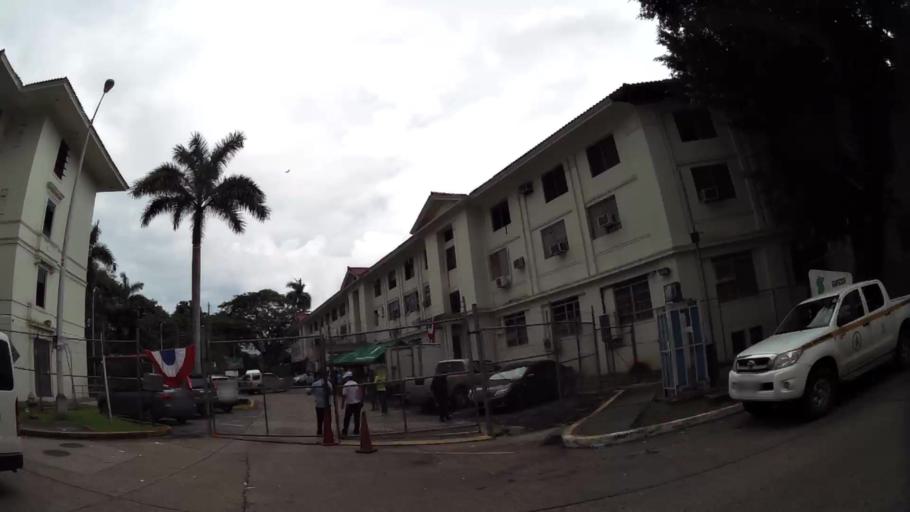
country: PA
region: Panama
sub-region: Distrito de Panama
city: Ancon
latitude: 8.9609
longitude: -79.5460
